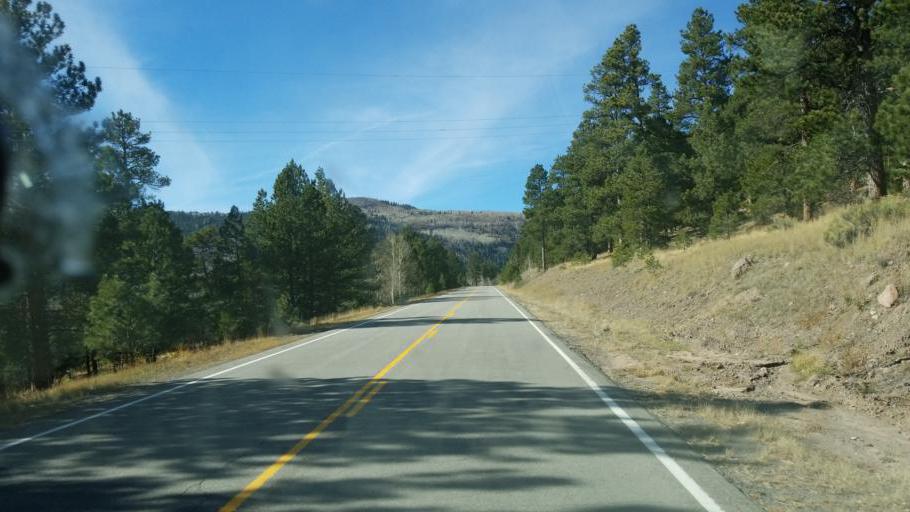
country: US
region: Colorado
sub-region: Conejos County
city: Conejos
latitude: 37.0770
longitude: -106.2894
